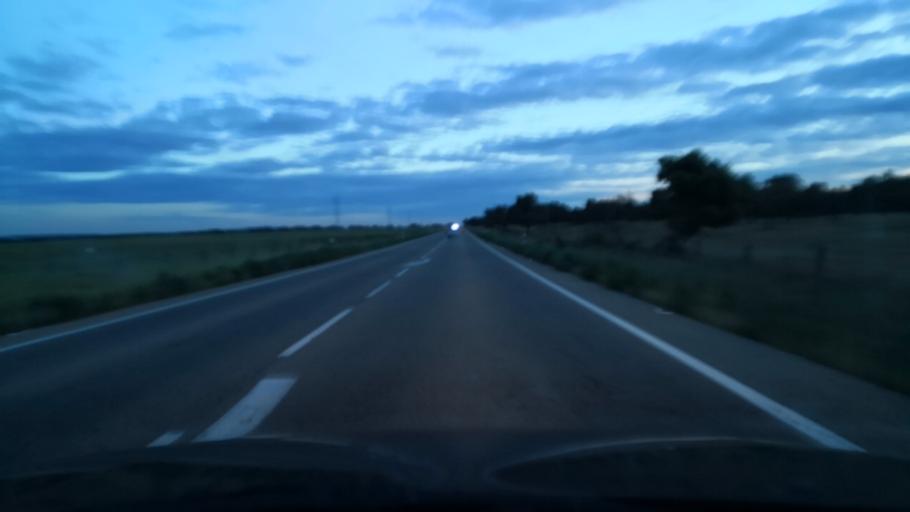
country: ES
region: Extremadura
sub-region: Provincia de Badajoz
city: Badajoz
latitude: 38.9575
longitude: -6.9056
